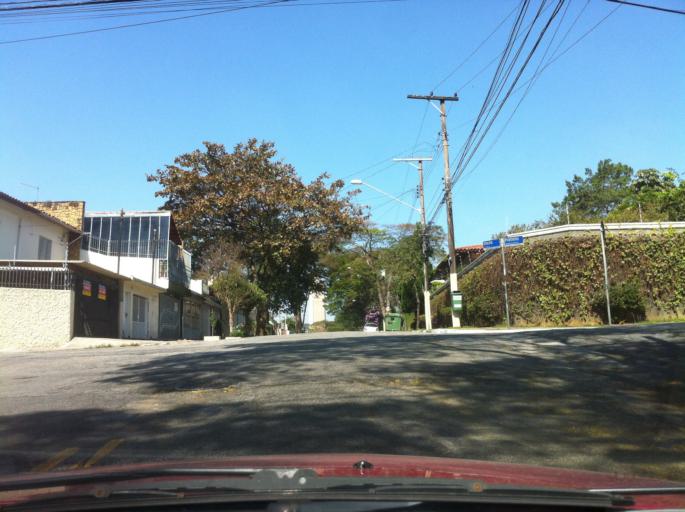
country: BR
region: Sao Paulo
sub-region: Sao Paulo
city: Sao Paulo
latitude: -23.6170
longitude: -46.6476
